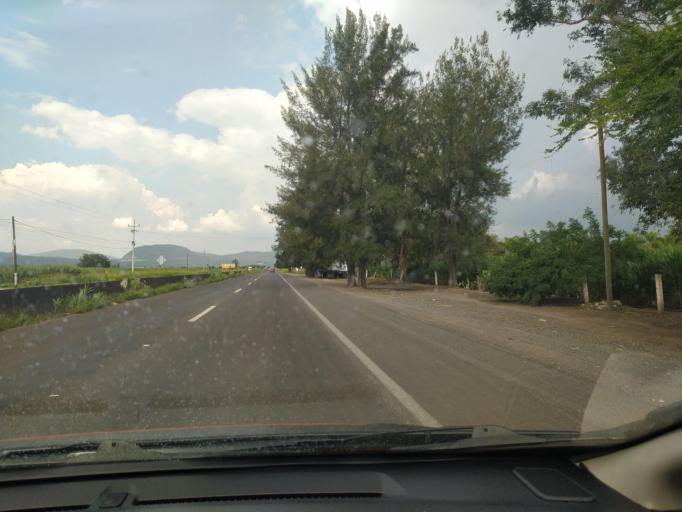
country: MX
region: Jalisco
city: Bellavista
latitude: 20.4120
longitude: -103.6391
